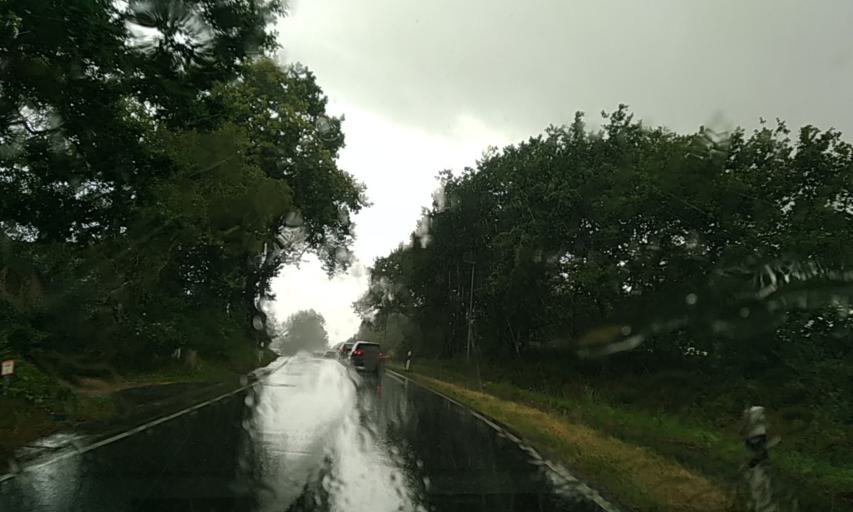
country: DE
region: Schleswig-Holstein
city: Lurschau
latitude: 54.5500
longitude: 9.4970
